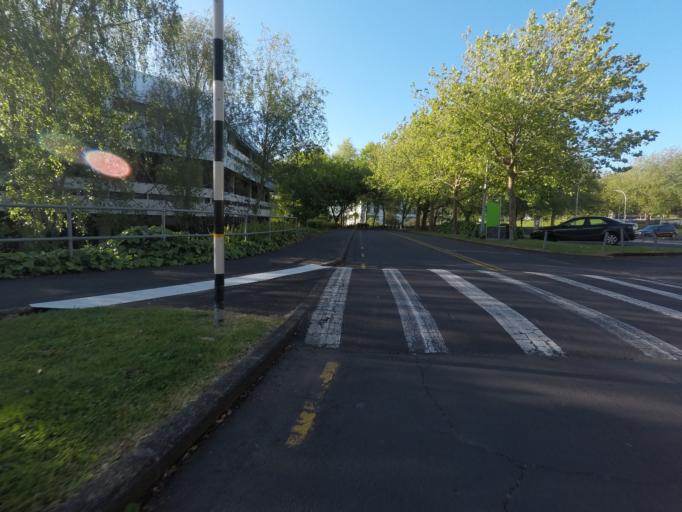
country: NZ
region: Auckland
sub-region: Auckland
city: Rosebank
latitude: -36.8815
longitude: 174.7097
